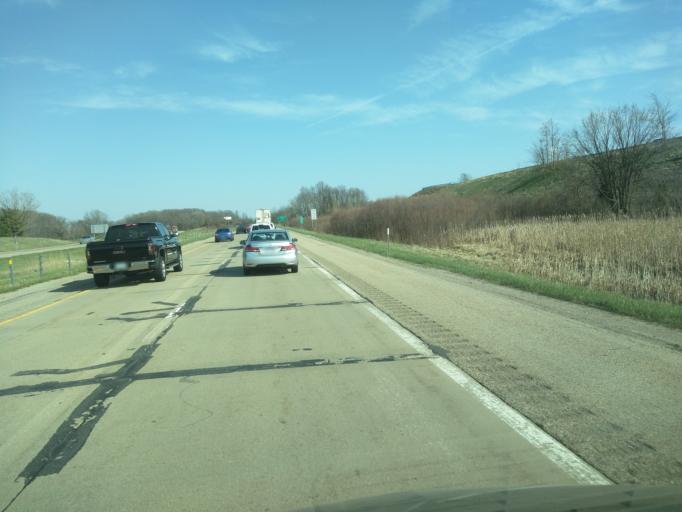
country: US
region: Michigan
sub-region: Kent County
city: Forest Hills
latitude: 42.8934
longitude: -85.5081
